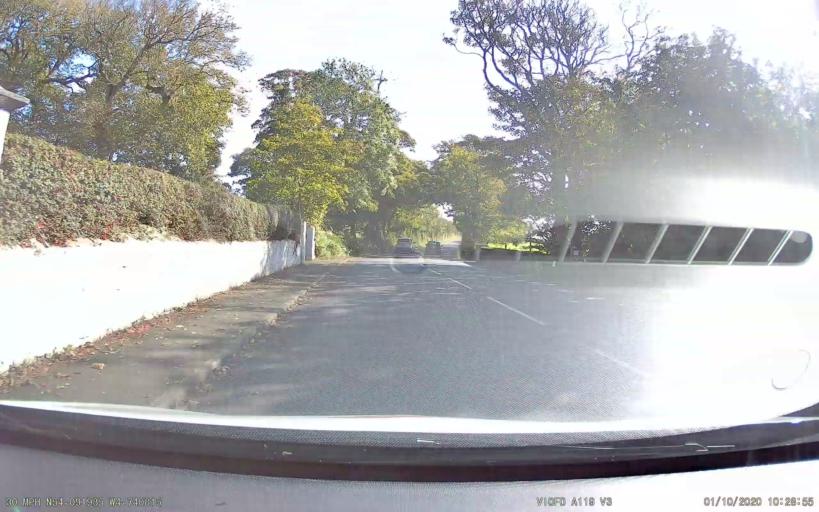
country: IM
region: Port Erin
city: Port Erin
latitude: 54.0919
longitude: -4.7408
